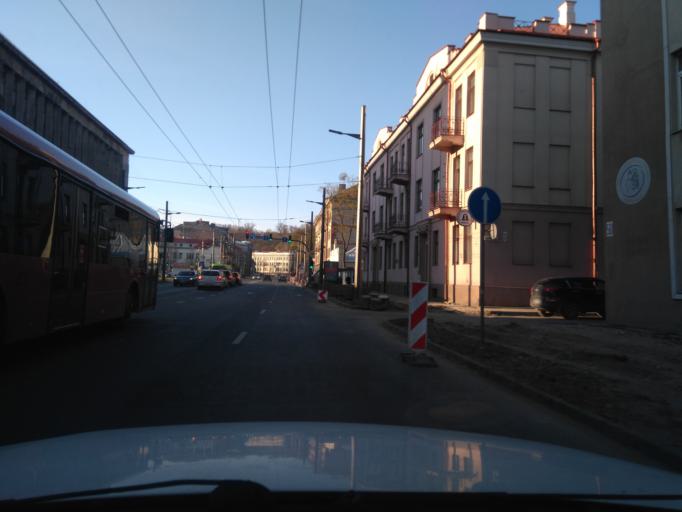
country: LT
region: Kauno apskritis
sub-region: Kaunas
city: Kaunas
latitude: 54.8944
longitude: 23.9251
